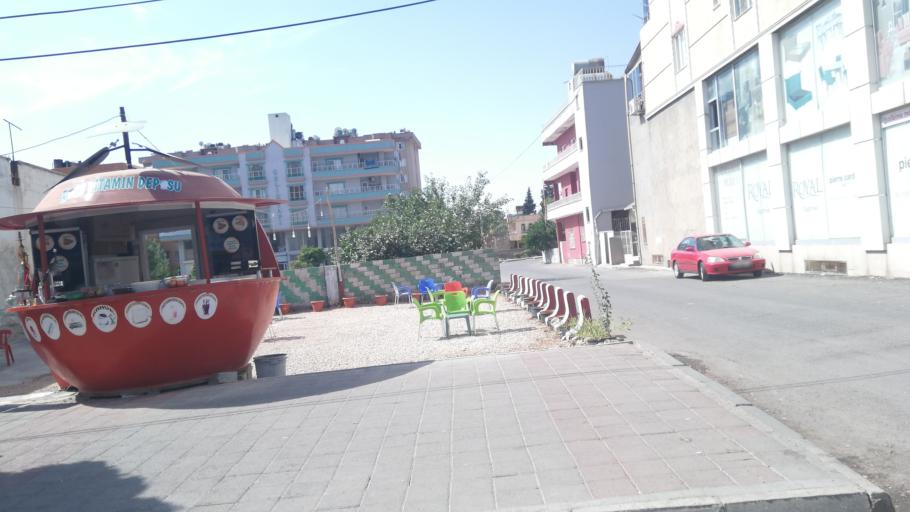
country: TR
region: Mardin
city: Midyat
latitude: 37.4235
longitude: 41.3436
